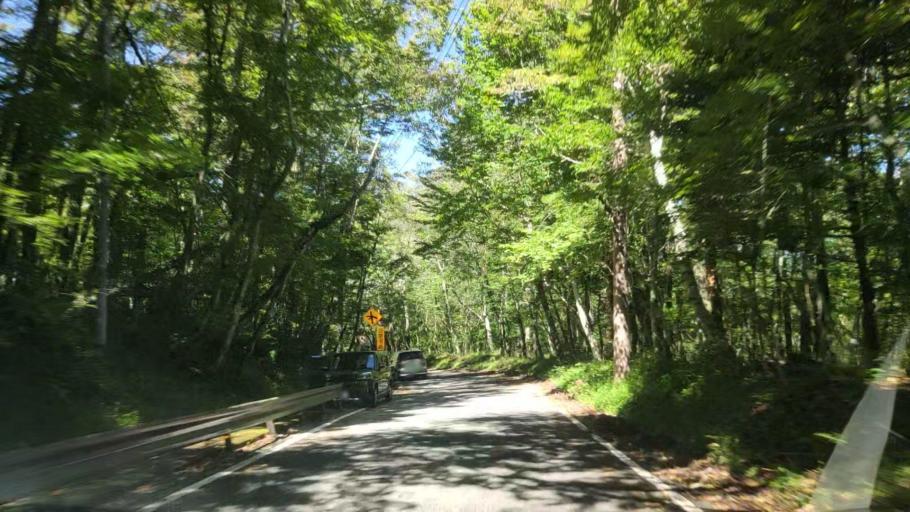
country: JP
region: Shizuoka
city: Gotemba
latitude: 35.4054
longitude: 138.8592
